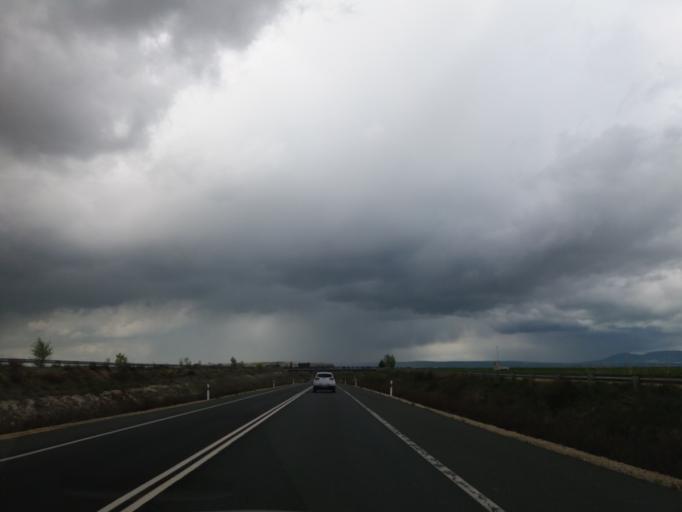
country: ES
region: La Rioja
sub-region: Provincia de La Rioja
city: Zarraton
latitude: 42.5437
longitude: -2.8766
